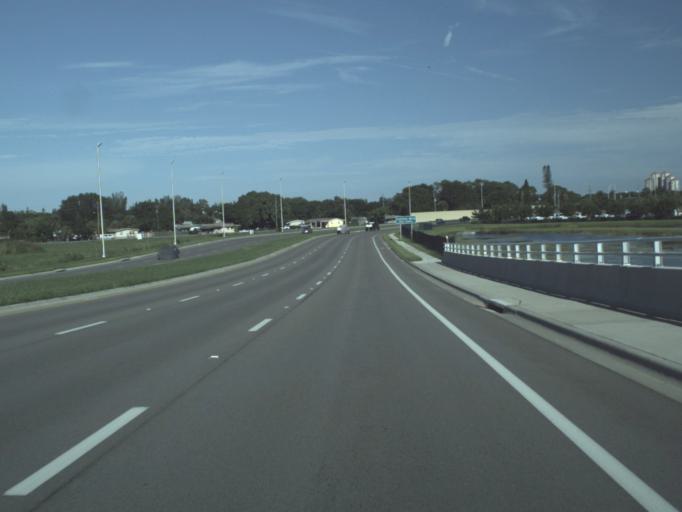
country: US
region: Florida
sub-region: Lee County
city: Fort Myers
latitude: 26.6140
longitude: -81.8572
